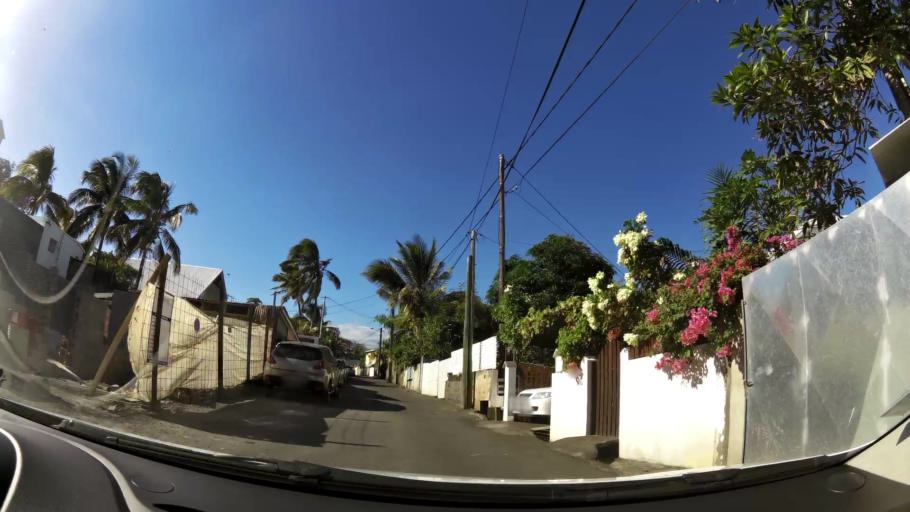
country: RE
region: Reunion
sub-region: Reunion
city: Saint-Pierre
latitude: -21.3459
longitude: 55.4822
